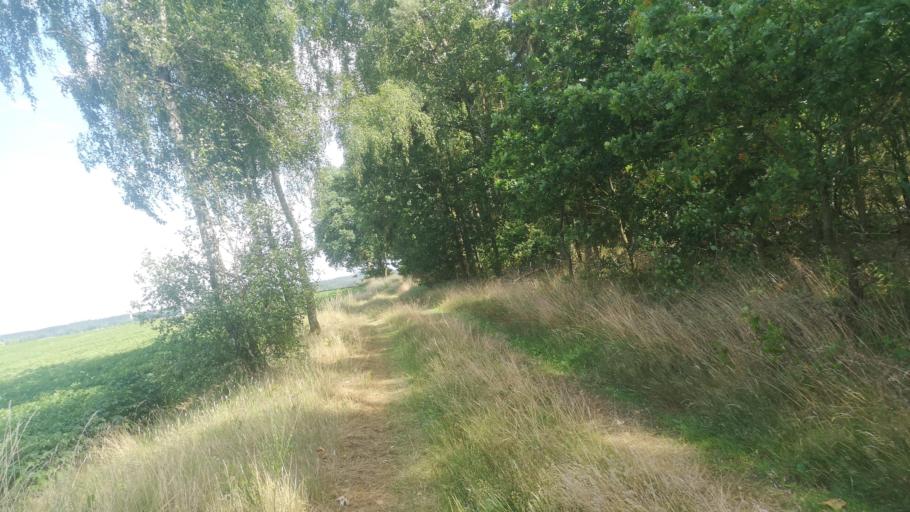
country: DE
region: Lower Saxony
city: Dahlem
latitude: 53.2233
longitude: 10.7443
